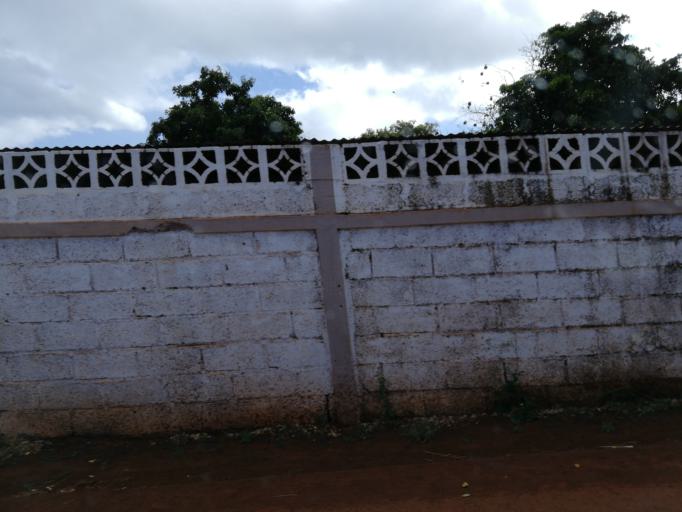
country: MU
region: Black River
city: Petite Riviere
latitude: -20.1922
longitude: 57.4642
